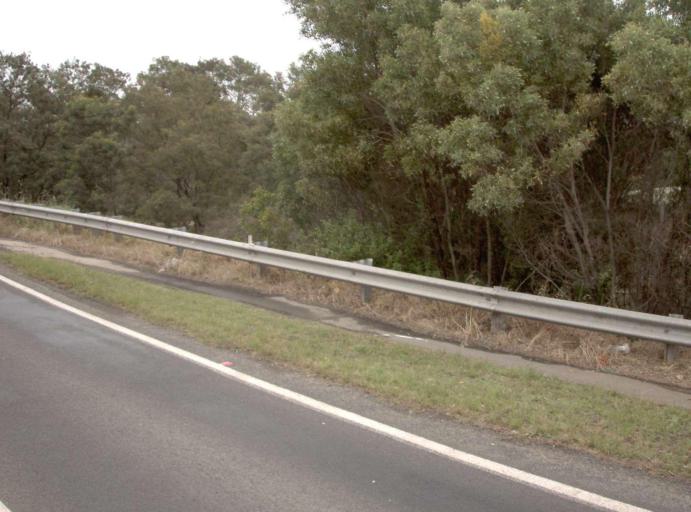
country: AU
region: Victoria
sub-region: Wellington
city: Sale
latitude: -37.9711
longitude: 147.0784
